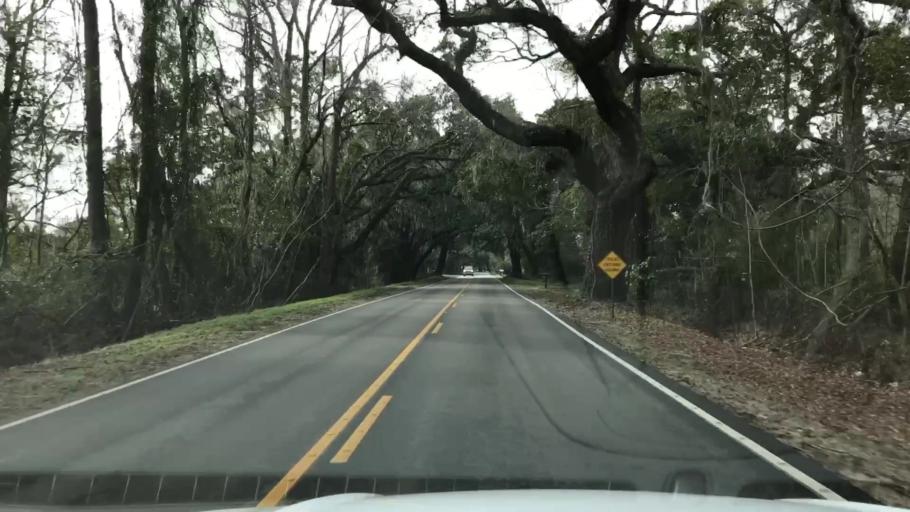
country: US
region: South Carolina
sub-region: Charleston County
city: Folly Beach
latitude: 32.6889
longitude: -80.0186
